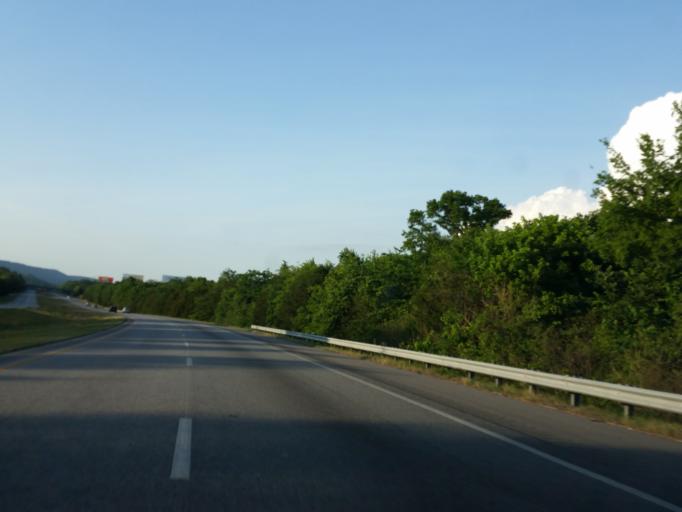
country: US
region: Georgia
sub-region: Dade County
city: Trenton
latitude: 34.8241
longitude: -85.5378
